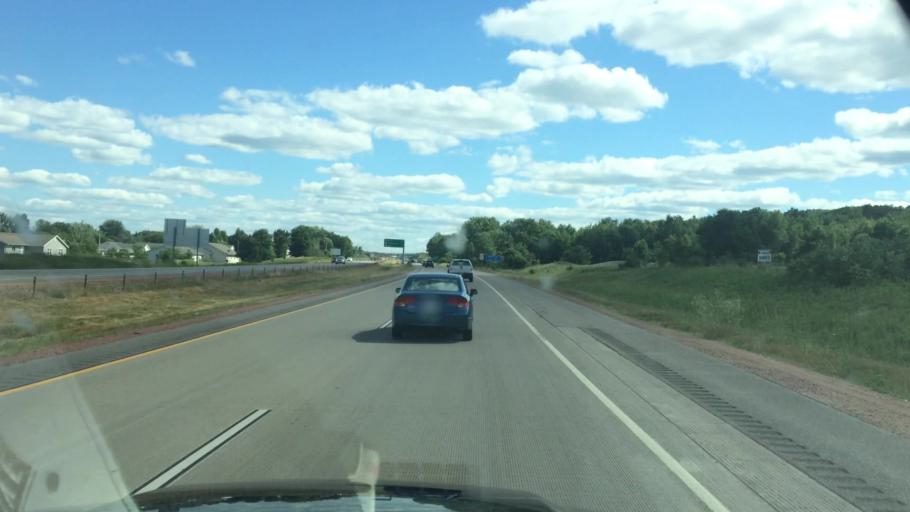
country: US
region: Wisconsin
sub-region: Marathon County
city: Wausau
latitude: 44.9807
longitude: -89.6575
